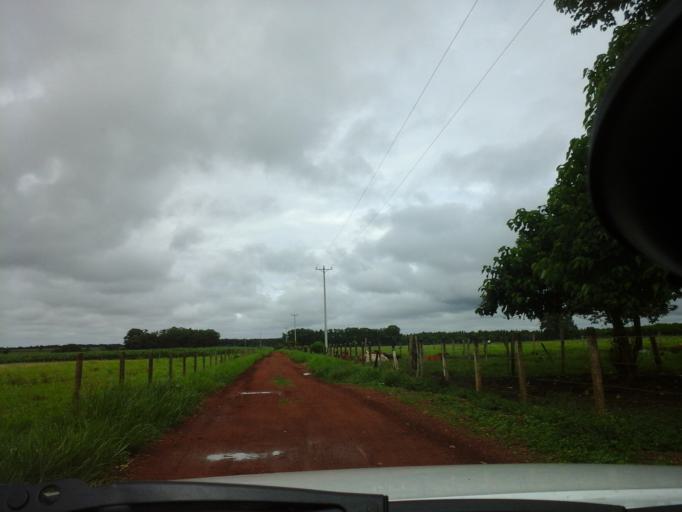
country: CO
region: Cundinamarca
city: Tibacuy
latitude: 4.2089
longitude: -72.4614
